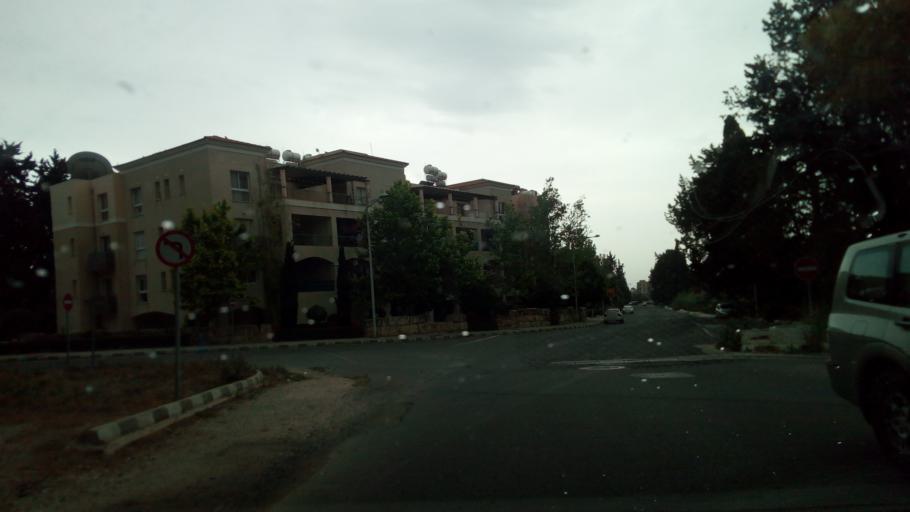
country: CY
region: Pafos
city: Paphos
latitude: 34.7667
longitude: 32.4300
